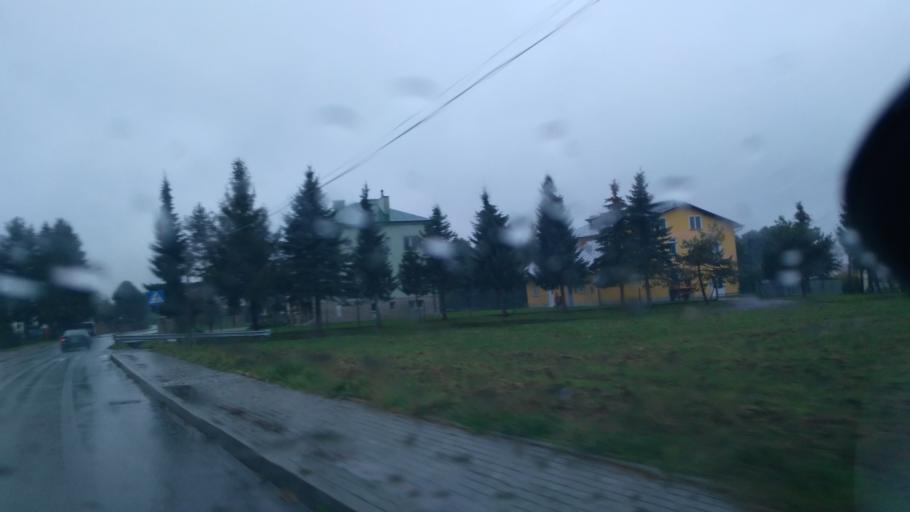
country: PL
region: Subcarpathian Voivodeship
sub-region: Powiat krosnienski
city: Korczyna
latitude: 49.7068
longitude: 21.8121
